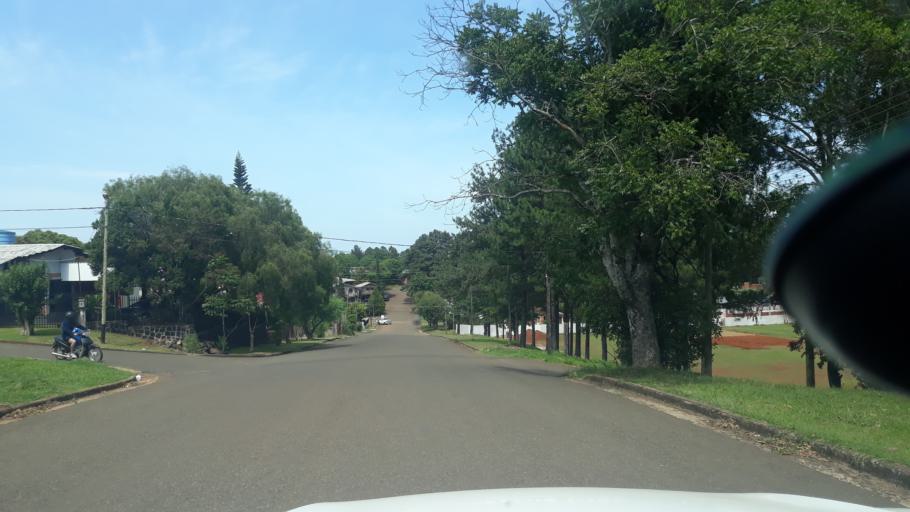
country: AR
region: Misiones
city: Bernardo de Irigoyen
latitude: -26.2518
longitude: -53.6477
